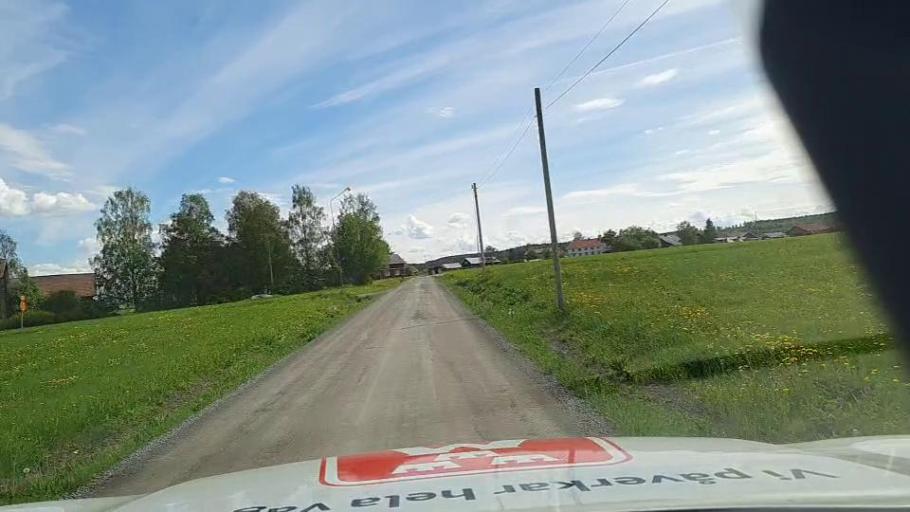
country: SE
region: Jaemtland
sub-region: OEstersunds Kommun
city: Brunflo
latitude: 62.9894
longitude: 14.8091
